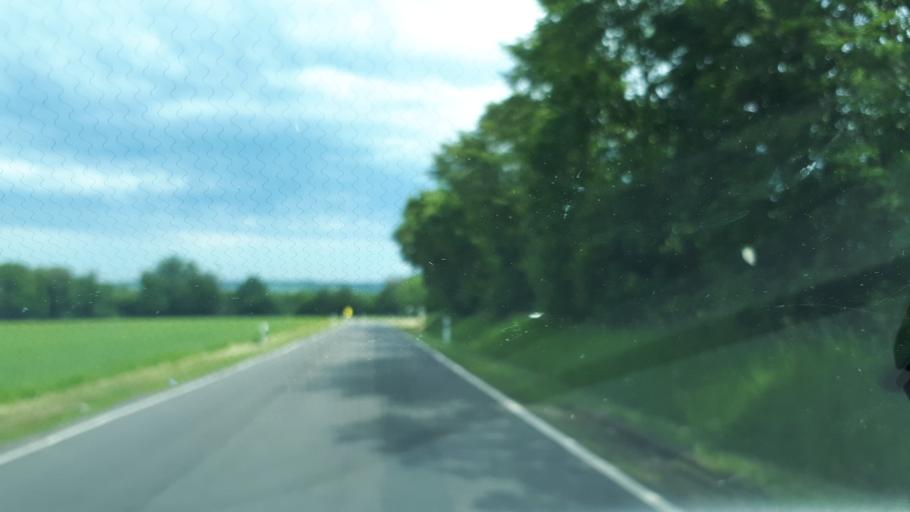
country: DE
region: Rheinland-Pfalz
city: Wagenhausen
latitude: 50.1341
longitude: 6.9716
